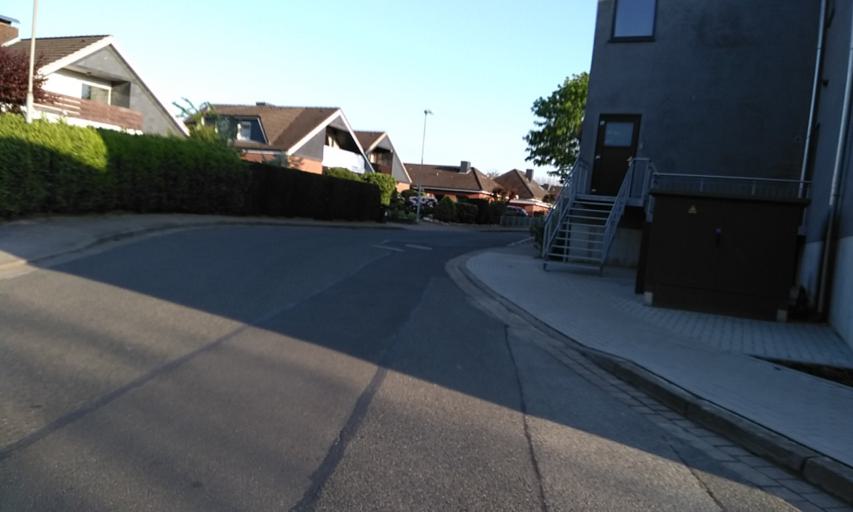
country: DE
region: Lower Saxony
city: Dollern
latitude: 53.5423
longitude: 9.5567
